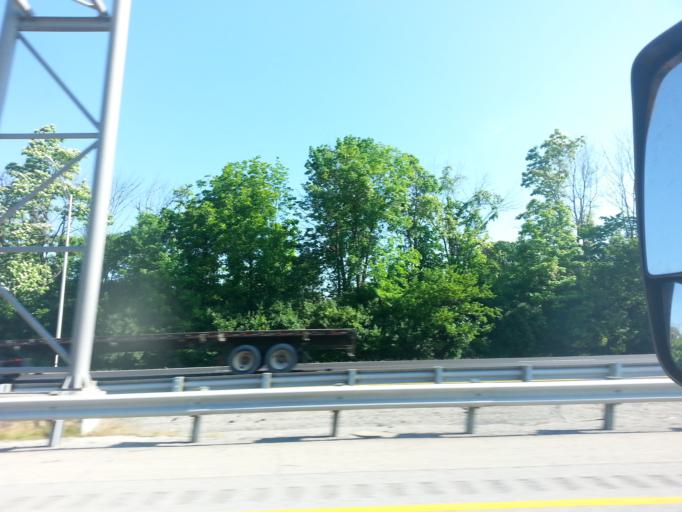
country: US
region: Kentucky
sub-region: Jefferson County
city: Middletown
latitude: 38.2228
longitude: -85.5105
